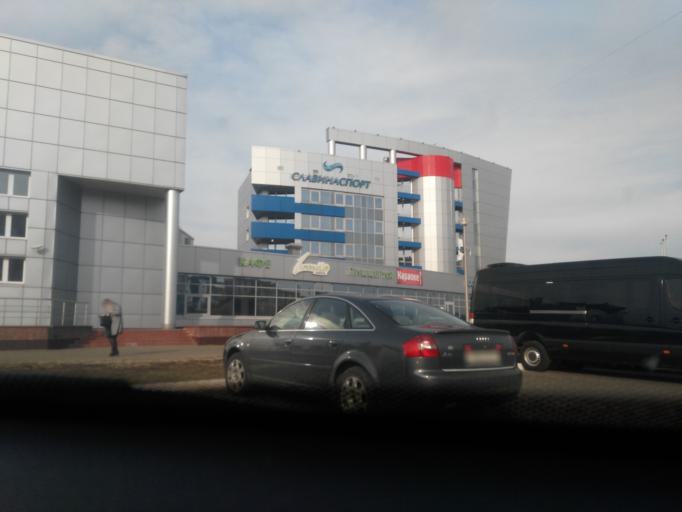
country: BY
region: Gomel
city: Zhlobin
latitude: 52.9084
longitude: 30.0508
